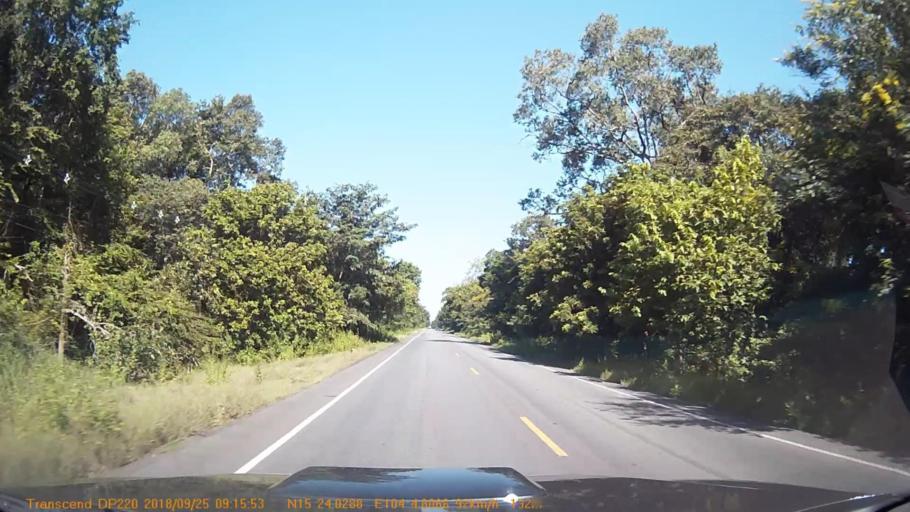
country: TH
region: Sisaket
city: Sila Lat
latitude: 15.4004
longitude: 104.0803
